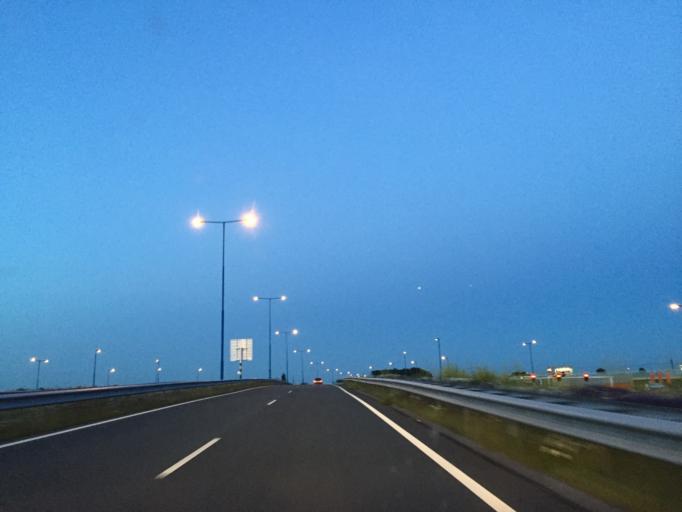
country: NL
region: South Holland
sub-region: Gemeente Rijnwoude
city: Benthuizen
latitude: 52.0497
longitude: 4.5364
